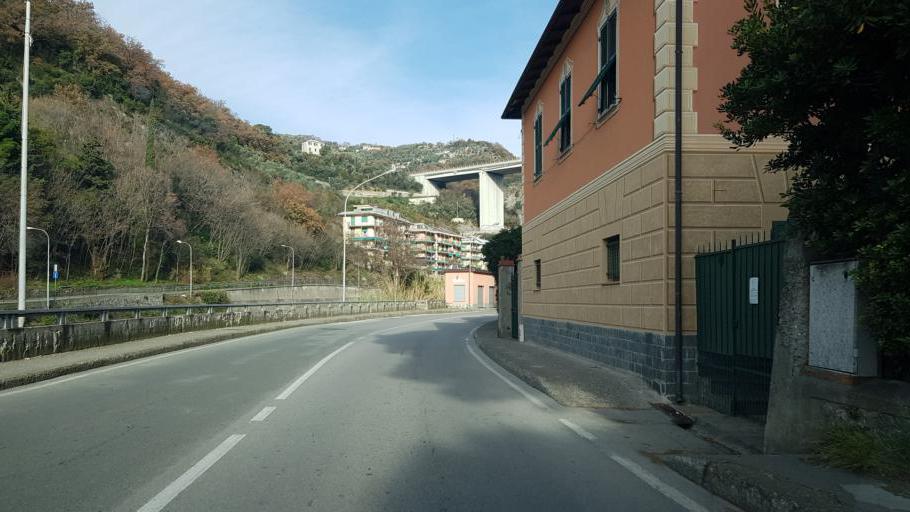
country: IT
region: Liguria
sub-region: Provincia di Genova
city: Recco
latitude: 44.3710
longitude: 9.1501
